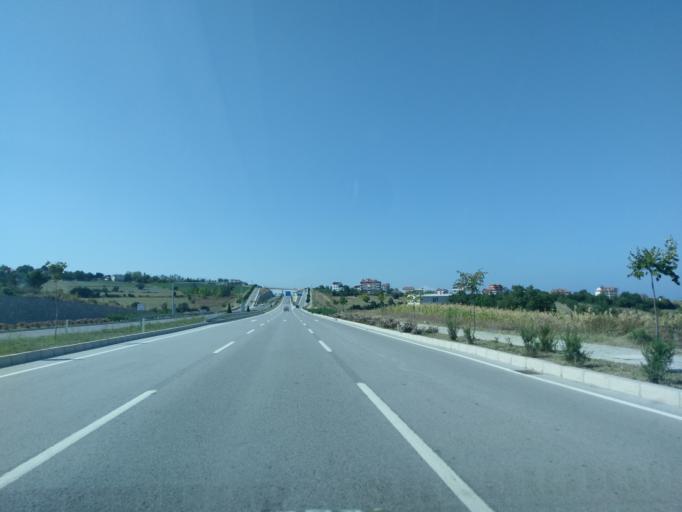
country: TR
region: Sinop
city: Gerze
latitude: 41.7926
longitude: 35.1881
